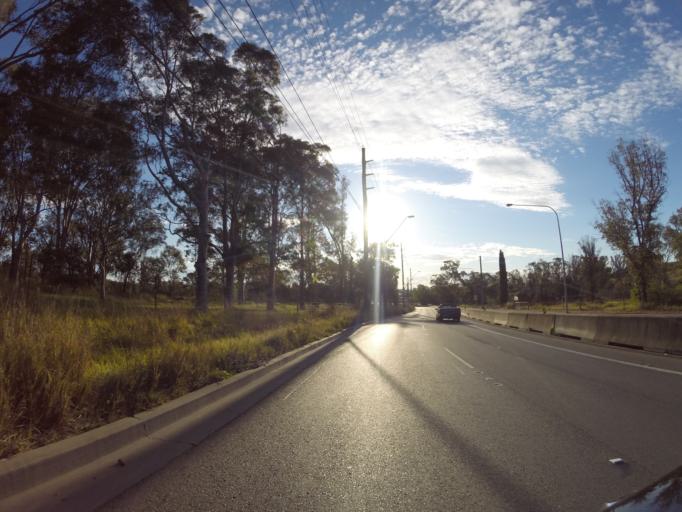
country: AU
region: New South Wales
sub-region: Fairfield
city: Horsley Park
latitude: -33.8453
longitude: 150.8675
